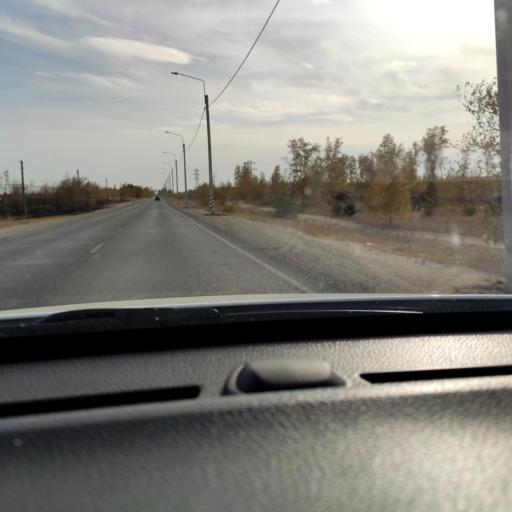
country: RU
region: Voronezj
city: Maslovka
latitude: 51.5821
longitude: 39.2475
